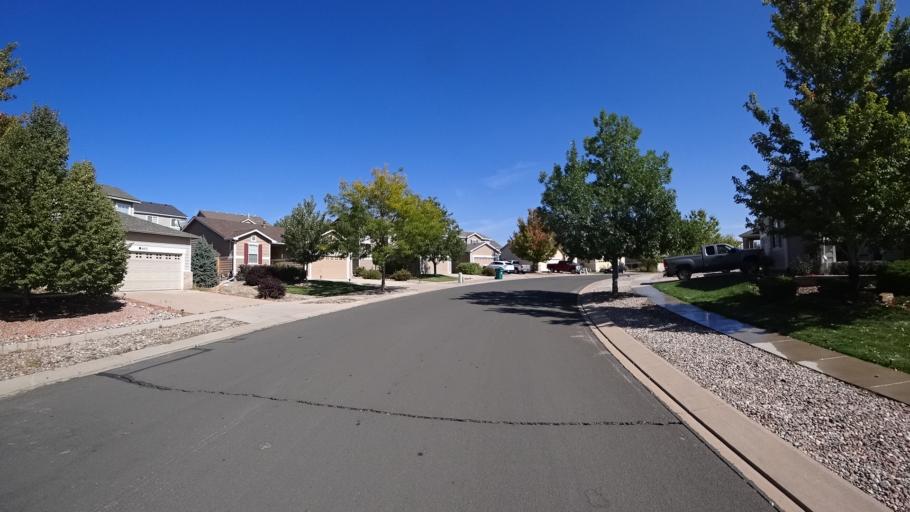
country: US
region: Colorado
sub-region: El Paso County
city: Cimarron Hills
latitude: 38.8962
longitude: -104.6946
